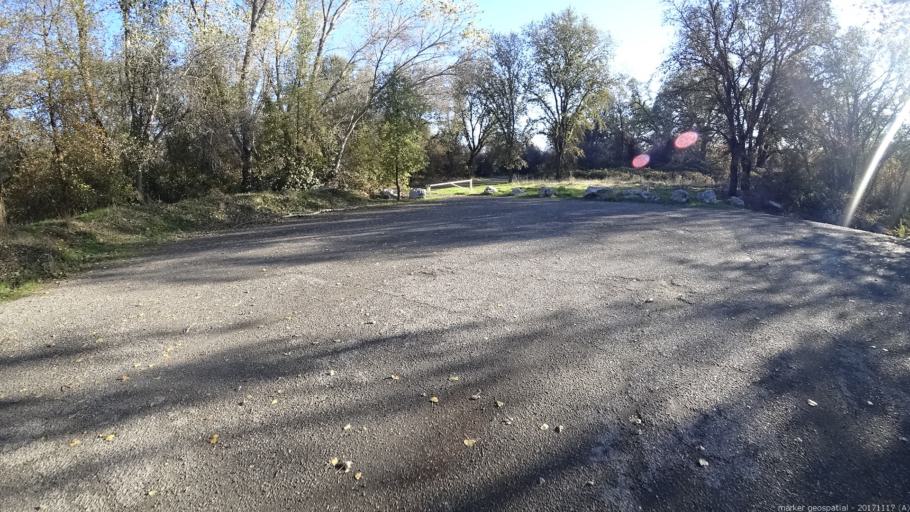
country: US
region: California
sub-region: Shasta County
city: Cottonwood
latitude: 40.3895
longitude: -122.1978
